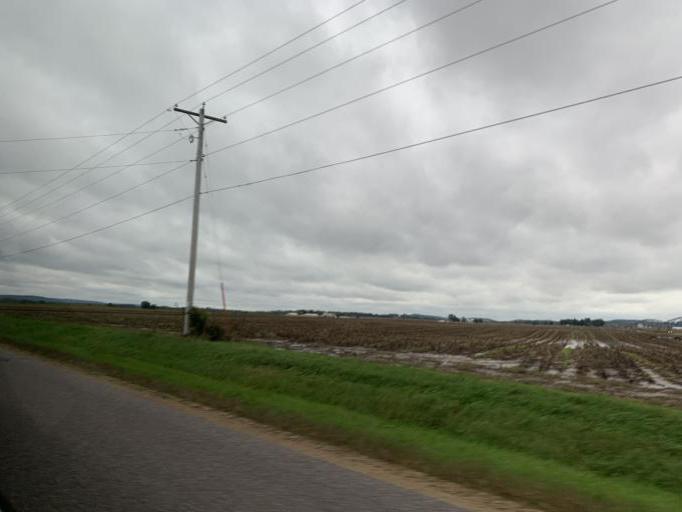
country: US
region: Wisconsin
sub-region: Sauk County
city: Prairie du Sac
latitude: 43.3154
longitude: -89.7769
